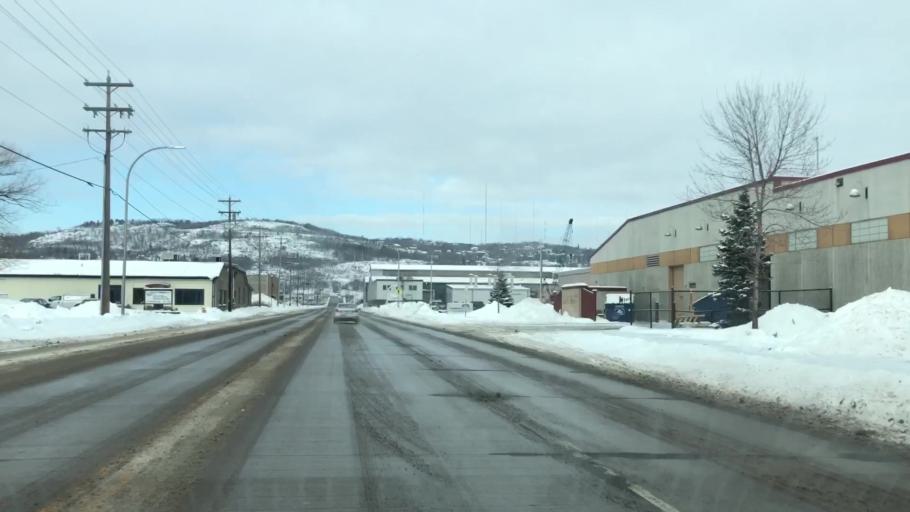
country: US
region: Minnesota
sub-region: Saint Louis County
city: Duluth
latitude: 46.7623
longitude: -92.1111
